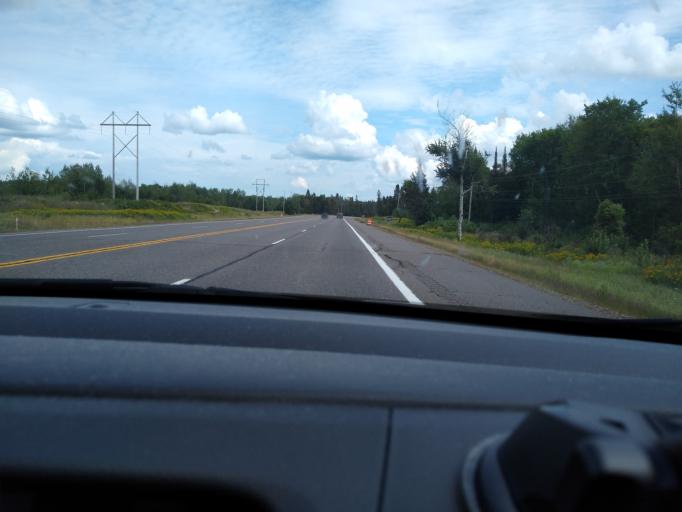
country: US
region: Michigan
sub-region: Marquette County
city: West Ishpeming
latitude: 46.5365
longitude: -88.0176
